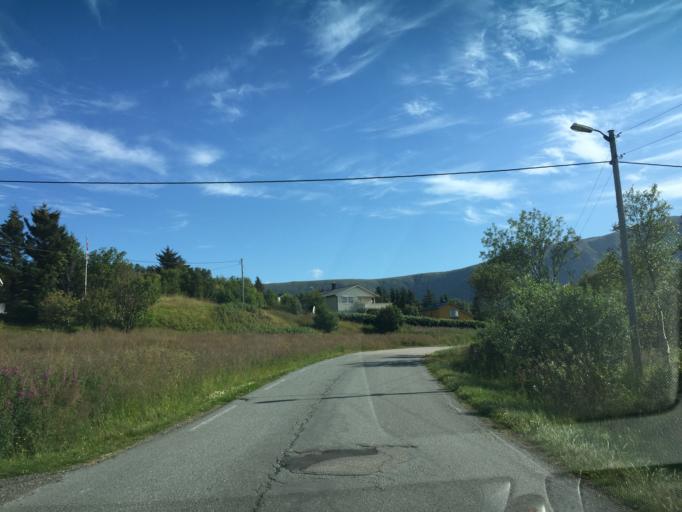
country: NO
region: Nordland
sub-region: Vagan
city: Kabelvag
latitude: 68.3918
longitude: 14.4403
